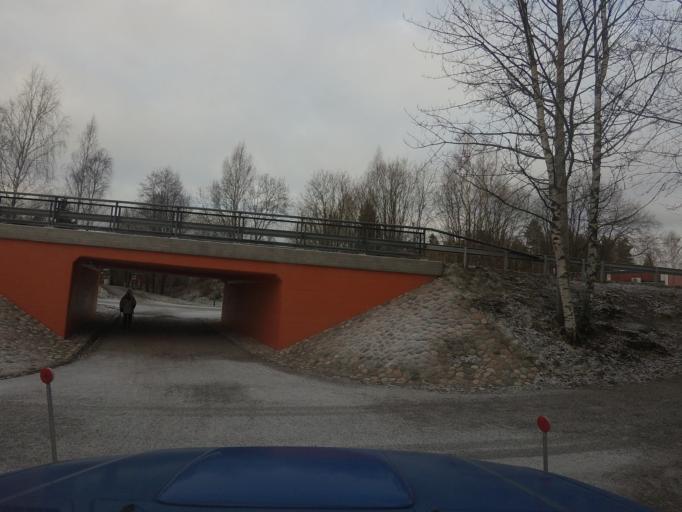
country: FI
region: Uusimaa
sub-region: Helsinki
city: Espoo
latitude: 60.1944
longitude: 24.6816
